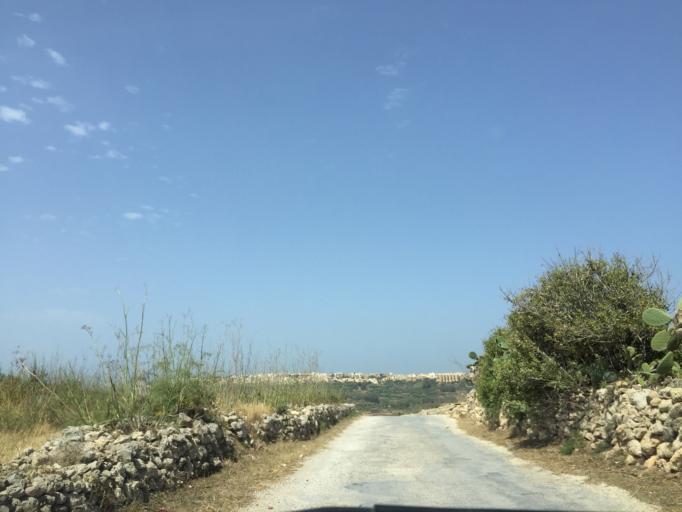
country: MT
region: In-Nadur
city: Nadur
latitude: 36.0538
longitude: 14.2934
